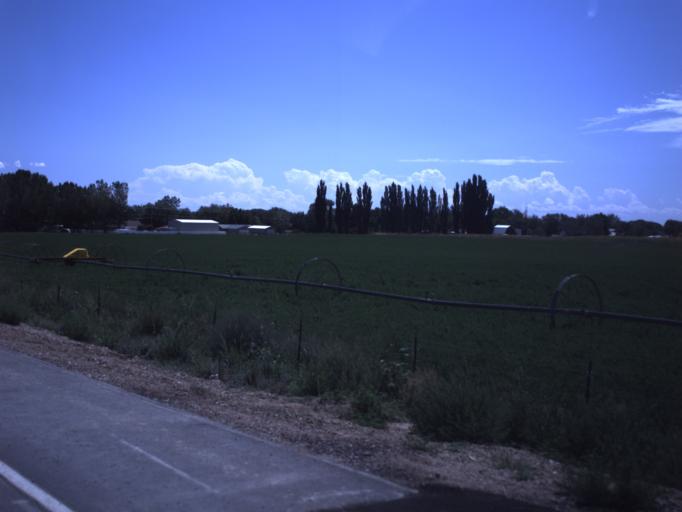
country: US
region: Utah
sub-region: Uintah County
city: Maeser
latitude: 40.4626
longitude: -109.5617
